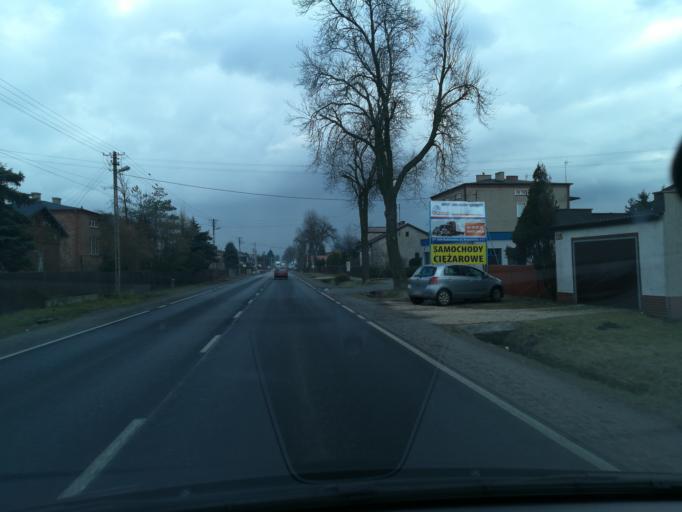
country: PL
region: Lodz Voivodeship
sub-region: Powiat radomszczanski
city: Radomsko
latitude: 51.0760
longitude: 19.4032
